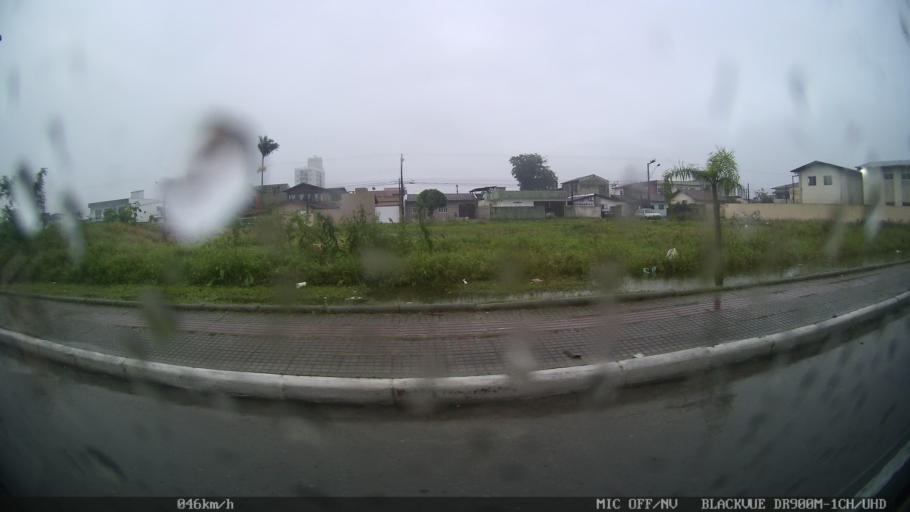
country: BR
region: Santa Catarina
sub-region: Itajai
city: Itajai
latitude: -26.9186
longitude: -48.6823
